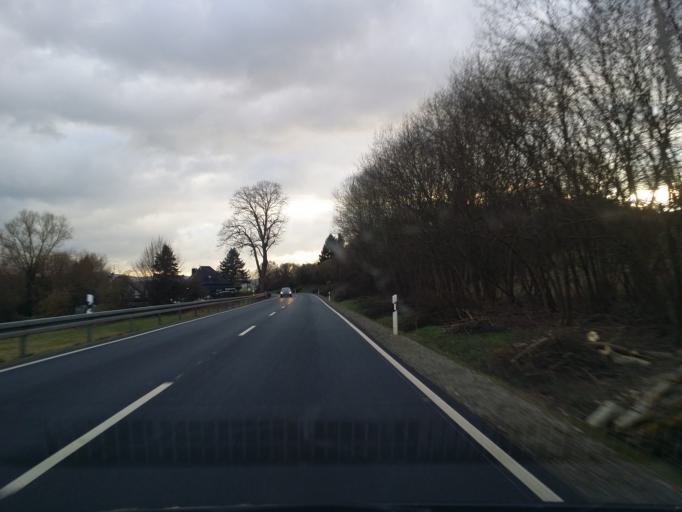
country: DE
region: Hesse
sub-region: Regierungsbezirk Darmstadt
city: Usingen
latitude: 50.3373
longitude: 8.5565
